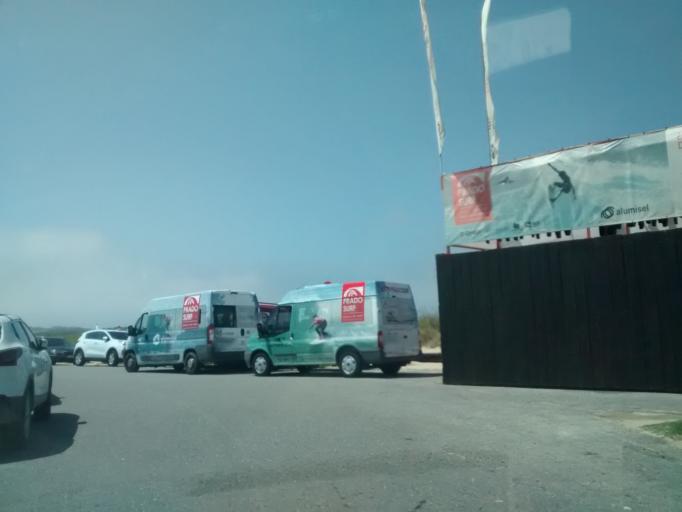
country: ES
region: Galicia
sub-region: Provincia de Pontevedra
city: O Grove
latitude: 42.4404
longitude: -8.8714
